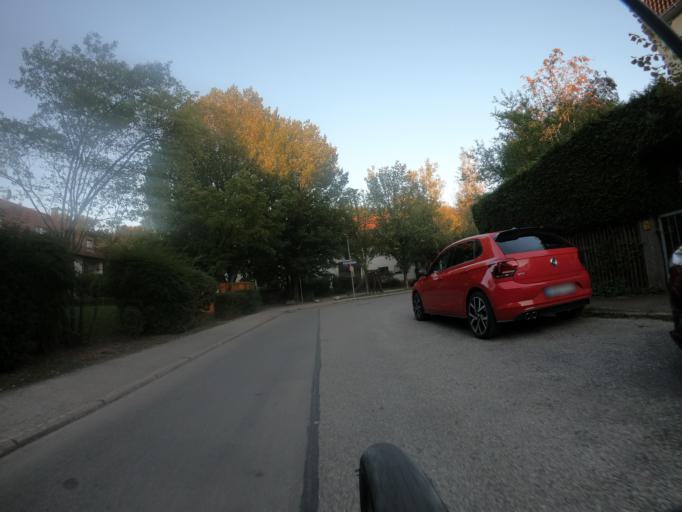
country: DE
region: Bavaria
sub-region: Upper Bavaria
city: Fuerstenfeldbruck
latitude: 48.1910
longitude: 11.2588
